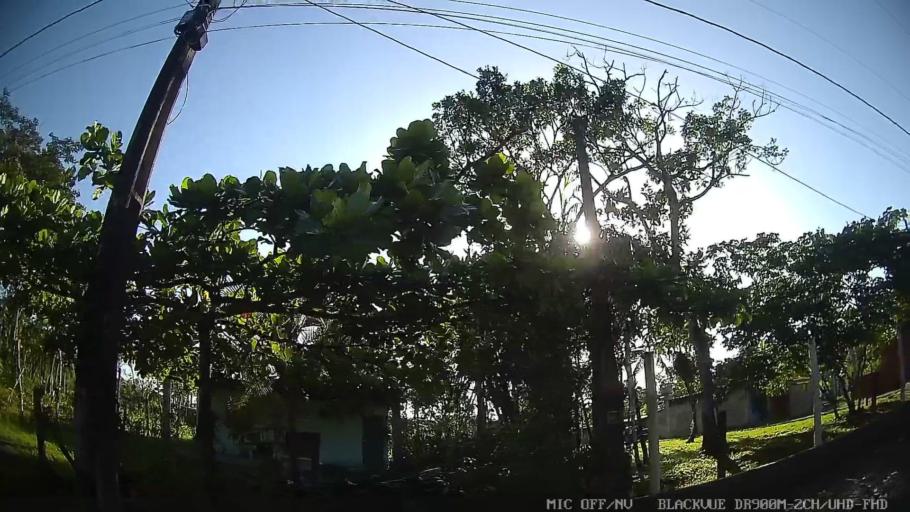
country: BR
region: Sao Paulo
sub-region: Itanhaem
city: Itanhaem
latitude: -24.1988
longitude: -46.8912
